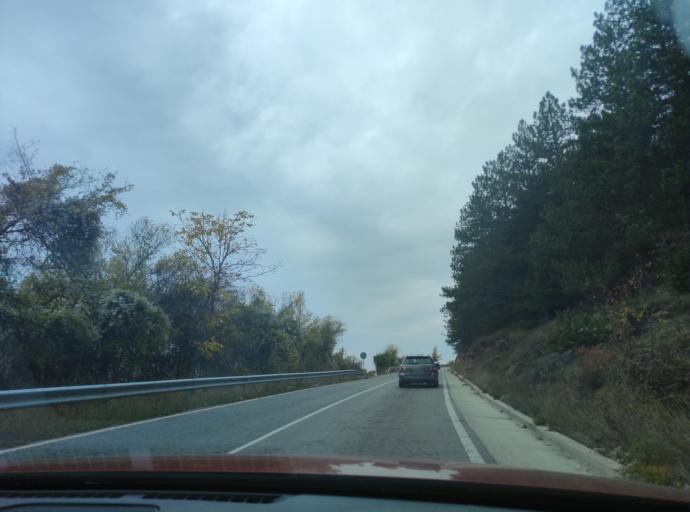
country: BG
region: Sofiya
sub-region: Obshtina Godech
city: Godech
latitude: 43.0378
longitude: 23.1347
